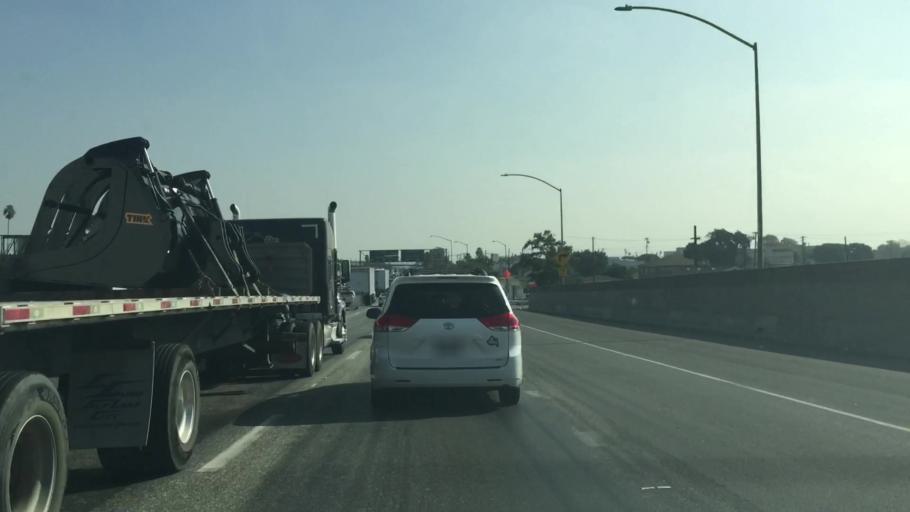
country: US
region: California
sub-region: Los Angeles County
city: East Los Angeles
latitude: 34.0200
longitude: -118.1907
